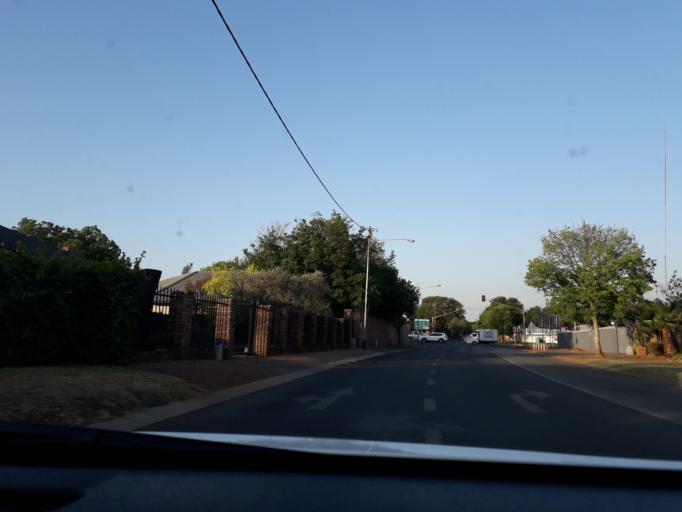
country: ZA
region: Gauteng
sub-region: City of Tshwane Metropolitan Municipality
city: Centurion
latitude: -25.8574
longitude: 28.2042
